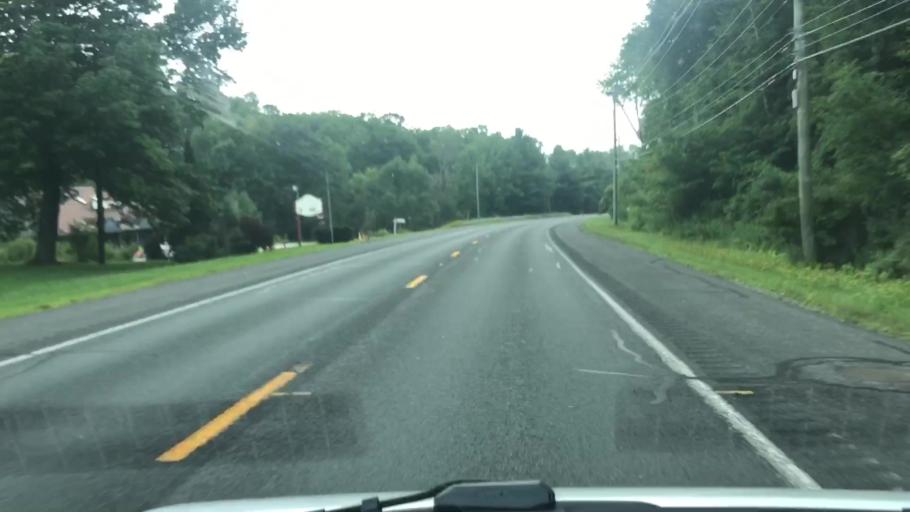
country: US
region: Massachusetts
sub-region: Berkshire County
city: Lanesborough
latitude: 42.5466
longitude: -73.2327
